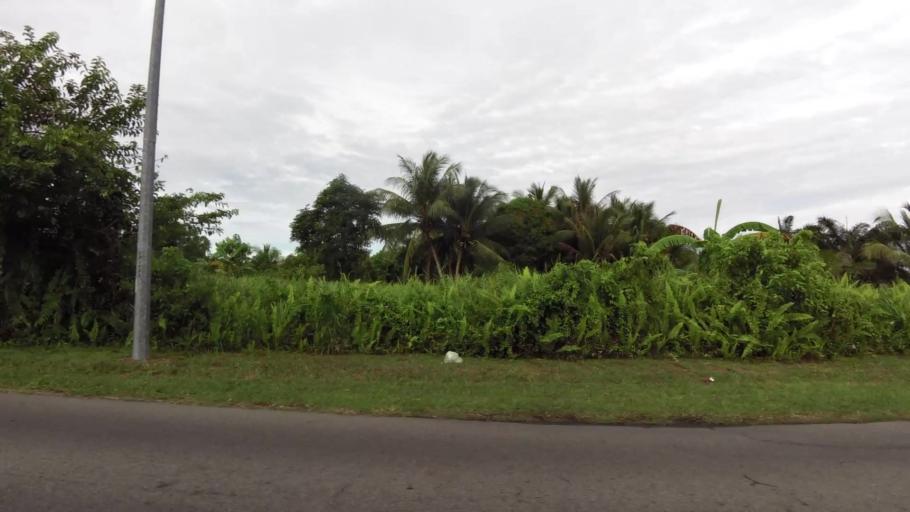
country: BN
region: Belait
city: Seria
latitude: 4.6044
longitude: 114.3254
